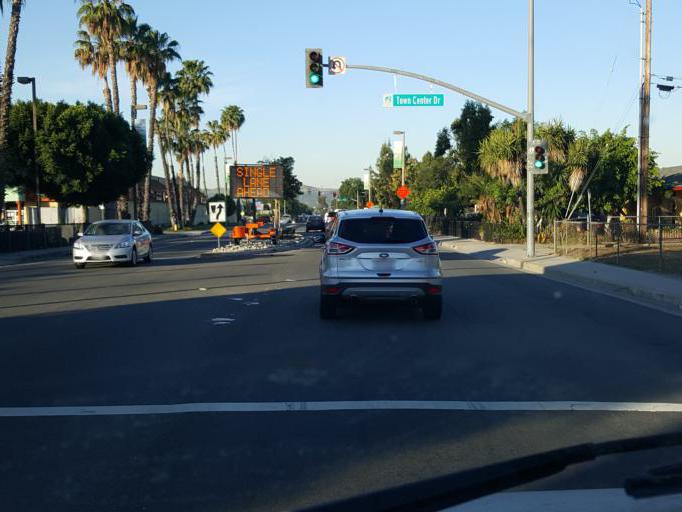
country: US
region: California
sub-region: Los Angeles County
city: Baldwin Park
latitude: 34.0731
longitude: -117.9590
